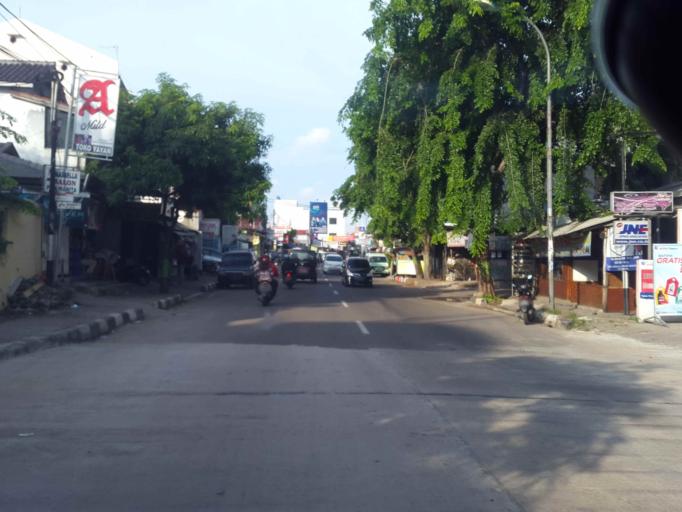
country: ID
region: West Java
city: Bekasi
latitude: -6.2489
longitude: 107.0006
